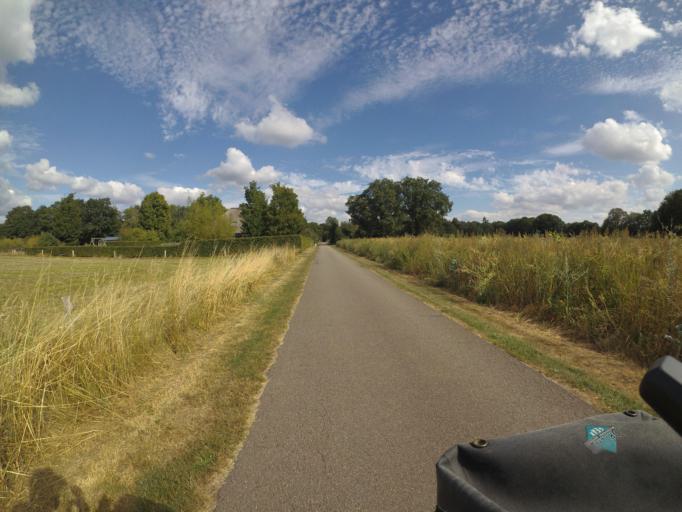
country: NL
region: Gelderland
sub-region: Gemeente Bronckhorst
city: Hengelo
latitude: 52.0933
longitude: 6.3090
